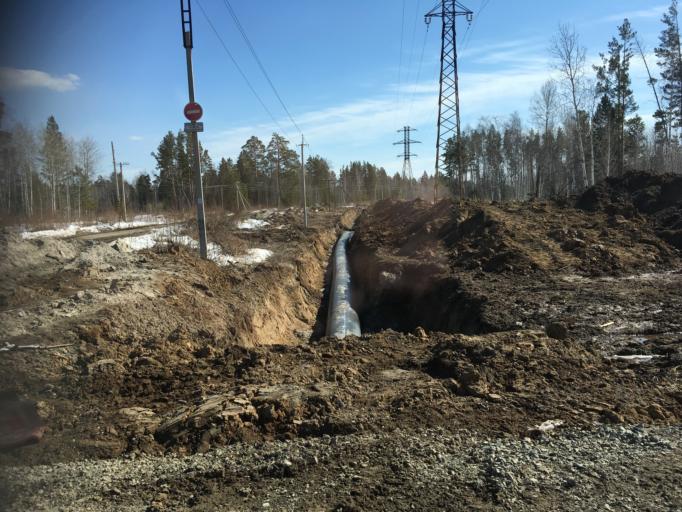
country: RU
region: Tomsk
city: Moryakovskiy Zaton
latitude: 56.6326
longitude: 84.6459
